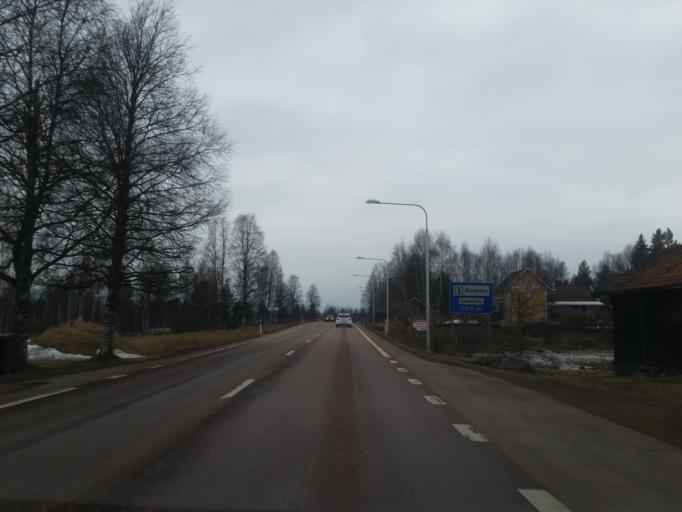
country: SE
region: Dalarna
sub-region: Alvdalens Kommun
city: AElvdalen
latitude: 61.2112
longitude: 14.0566
